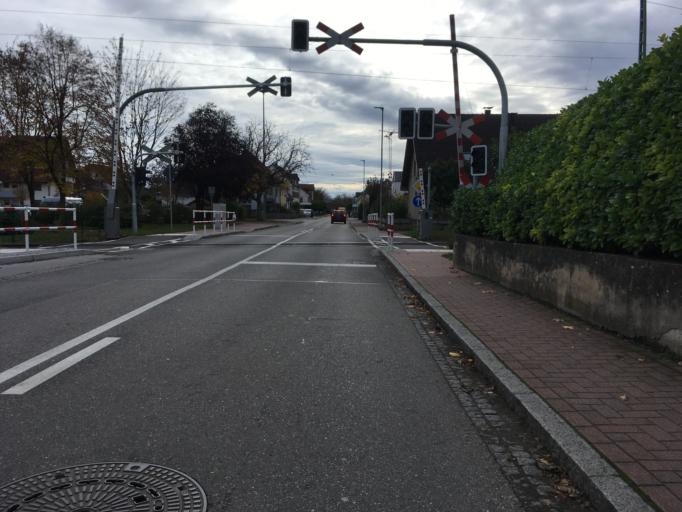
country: DE
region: Baden-Wuerttemberg
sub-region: Freiburg Region
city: Ihringen
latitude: 48.0404
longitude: 7.6477
